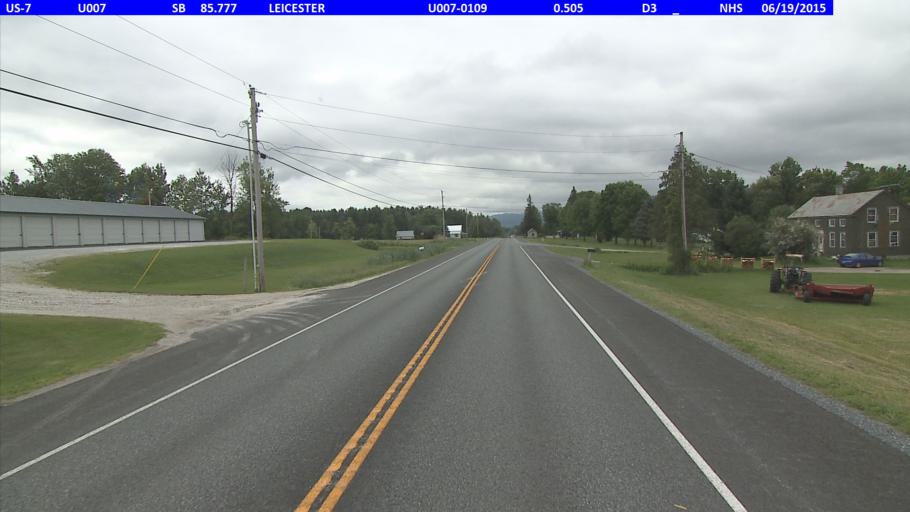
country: US
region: Vermont
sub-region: Rutland County
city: Brandon
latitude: 43.8516
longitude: -73.1063
